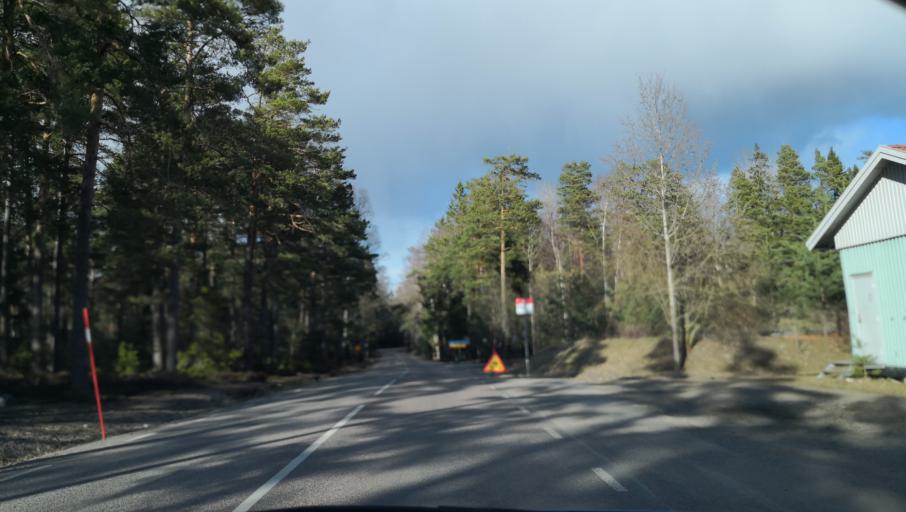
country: SE
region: Stockholm
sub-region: Varmdo Kommun
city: Mortnas
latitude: 59.2765
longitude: 18.4739
